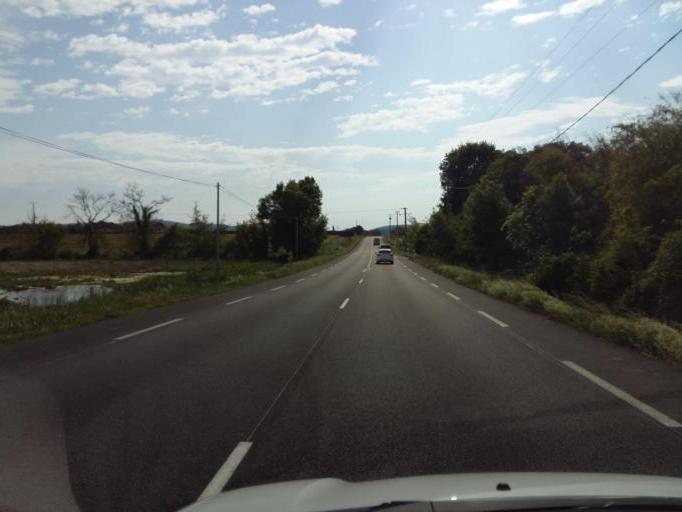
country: FR
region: Rhone-Alpes
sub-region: Departement de la Drome
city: Suze-la-Rousse
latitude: 44.2833
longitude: 4.8094
